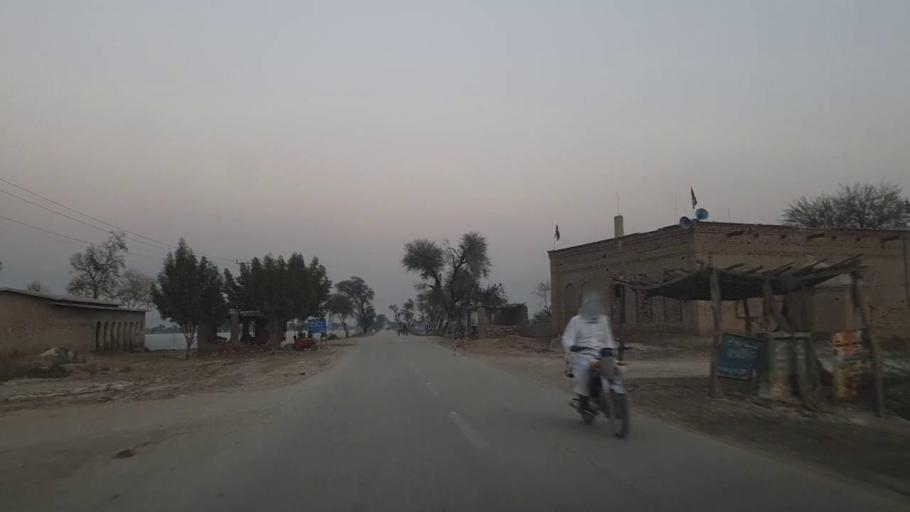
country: PK
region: Sindh
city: Naushahro Firoz
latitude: 26.8486
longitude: 68.0541
